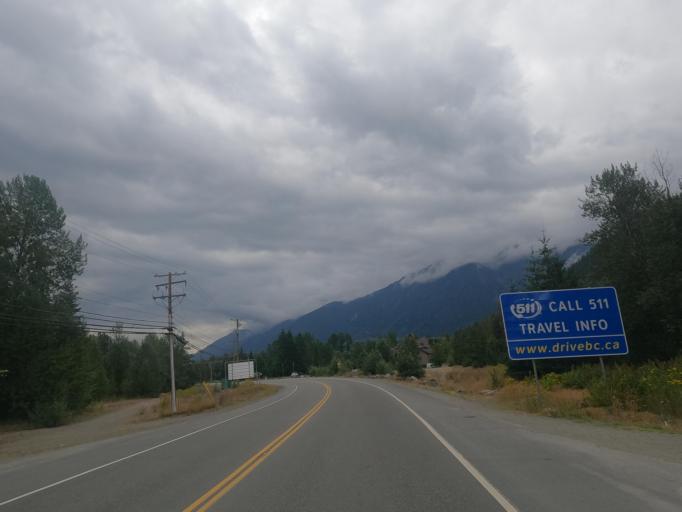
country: CA
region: British Columbia
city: Pemberton
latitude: 50.3164
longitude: -122.7959
